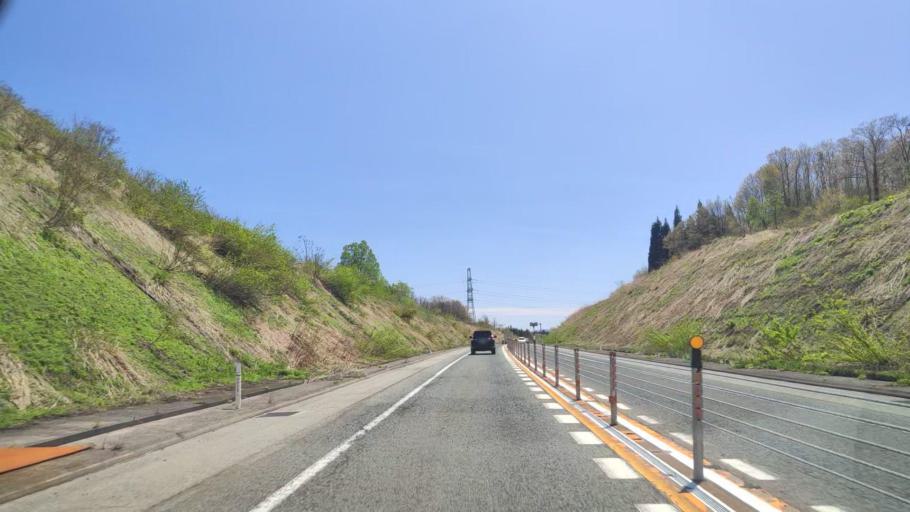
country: JP
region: Yamagata
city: Shinjo
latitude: 38.7212
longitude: 140.3087
